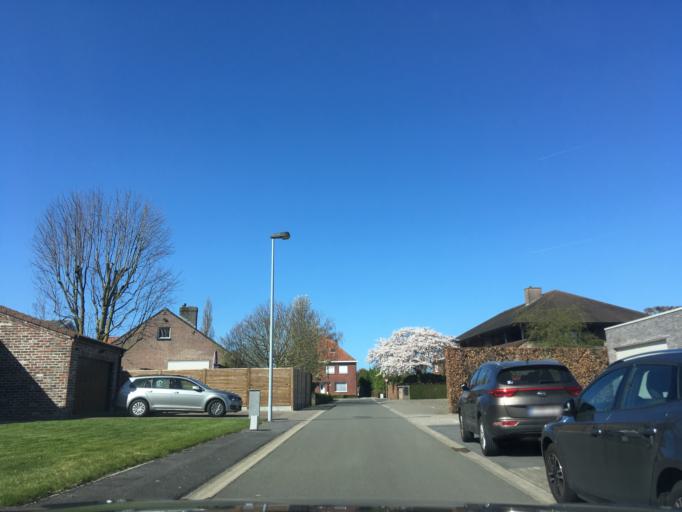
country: BE
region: Flanders
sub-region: Provincie West-Vlaanderen
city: Hooglede
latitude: 50.9804
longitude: 3.0911
